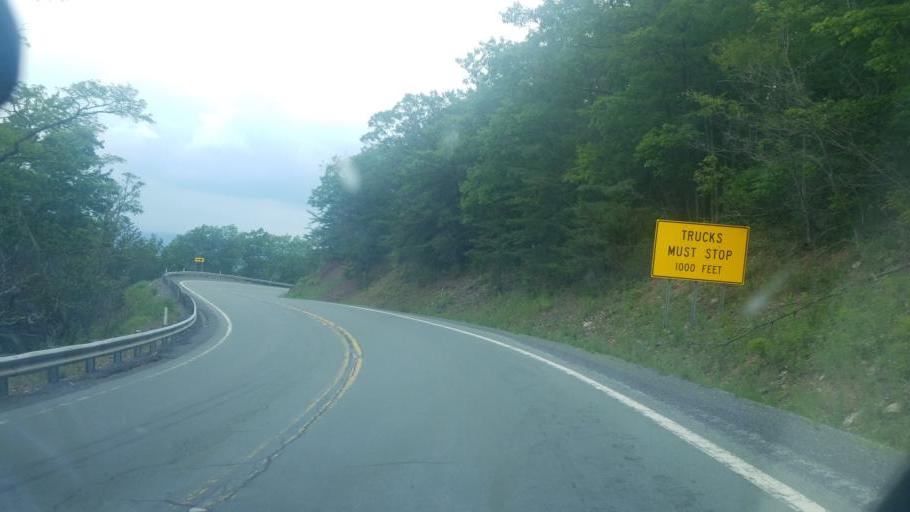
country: US
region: West Virginia
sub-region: Pendleton County
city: Franklin
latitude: 38.5825
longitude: -79.1665
